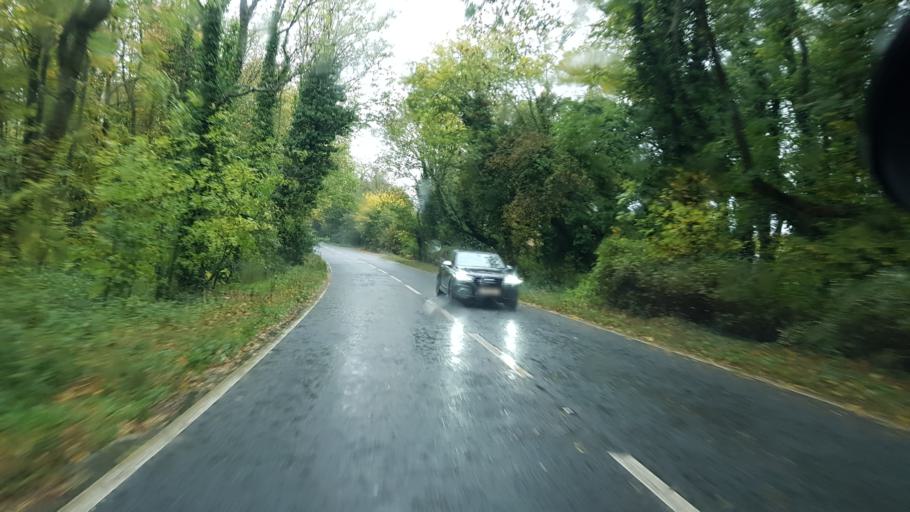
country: GB
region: England
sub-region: Gloucestershire
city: Stow on the Wold
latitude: 51.9037
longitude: -1.7150
